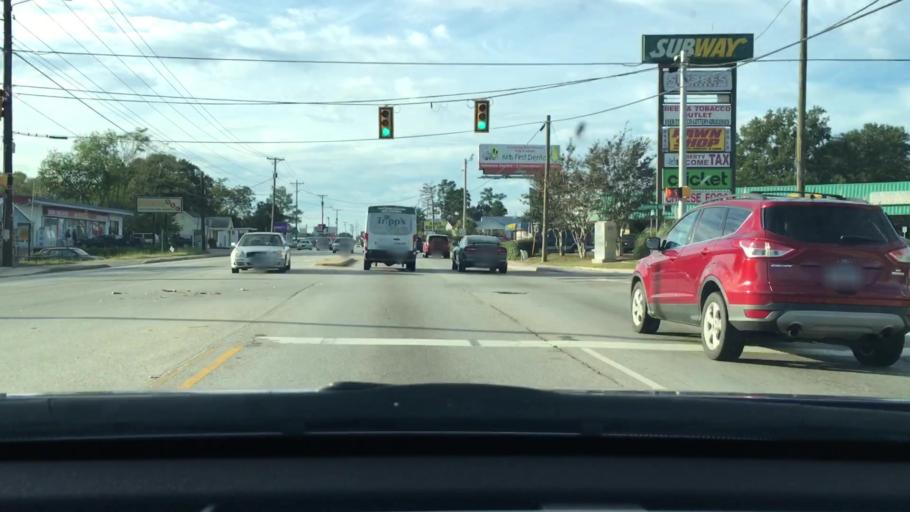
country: US
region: South Carolina
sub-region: Lexington County
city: Saint Andrews
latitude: 34.0448
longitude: -81.1001
